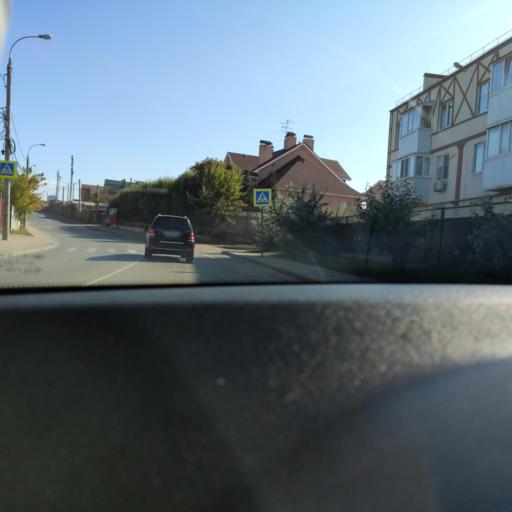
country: RU
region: Samara
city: Samara
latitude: 53.2682
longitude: 50.1986
